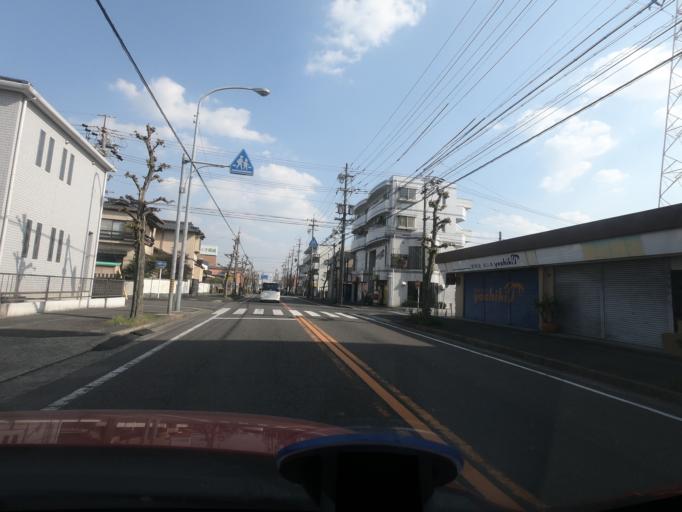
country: JP
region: Aichi
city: Kasugai
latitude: 35.2446
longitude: 136.9644
